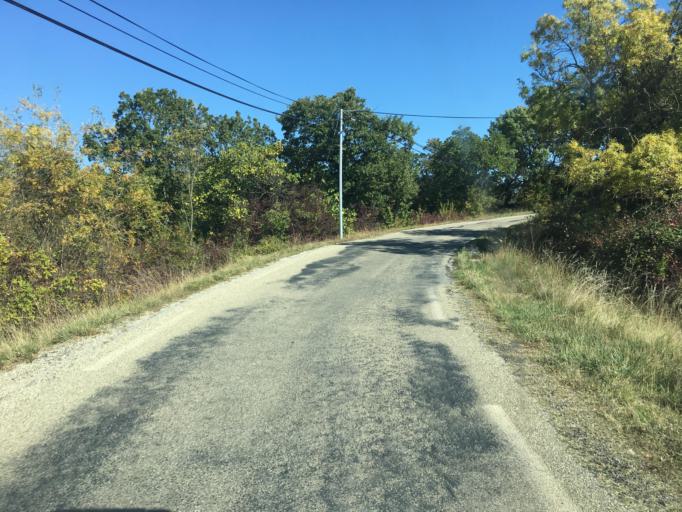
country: FR
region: Languedoc-Roussillon
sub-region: Departement du Gard
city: Mons
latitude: 44.1639
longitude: 4.3130
